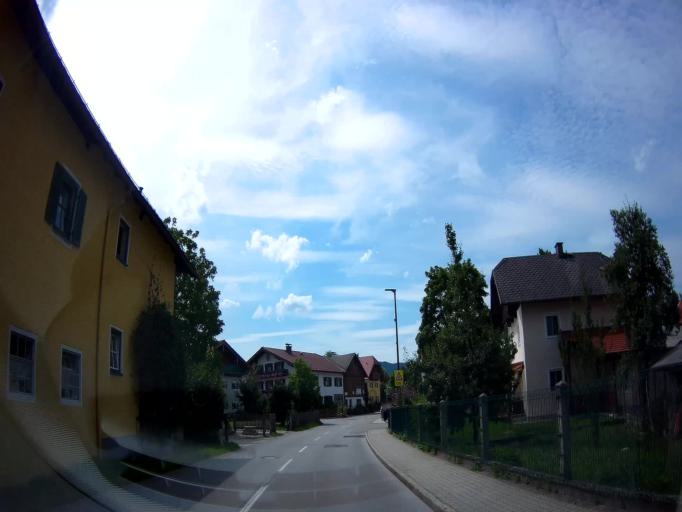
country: DE
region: Bavaria
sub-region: Upper Bavaria
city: Ainring
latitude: 47.7904
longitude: 12.9673
